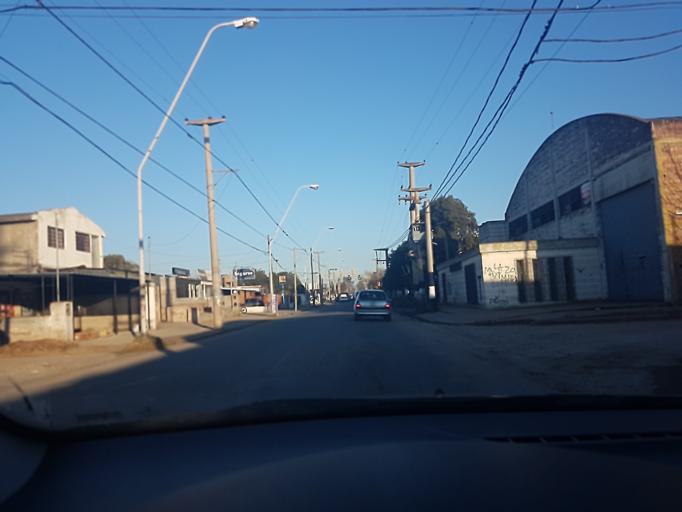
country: AR
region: Cordoba
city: Villa Allende
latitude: -31.3433
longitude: -64.2408
